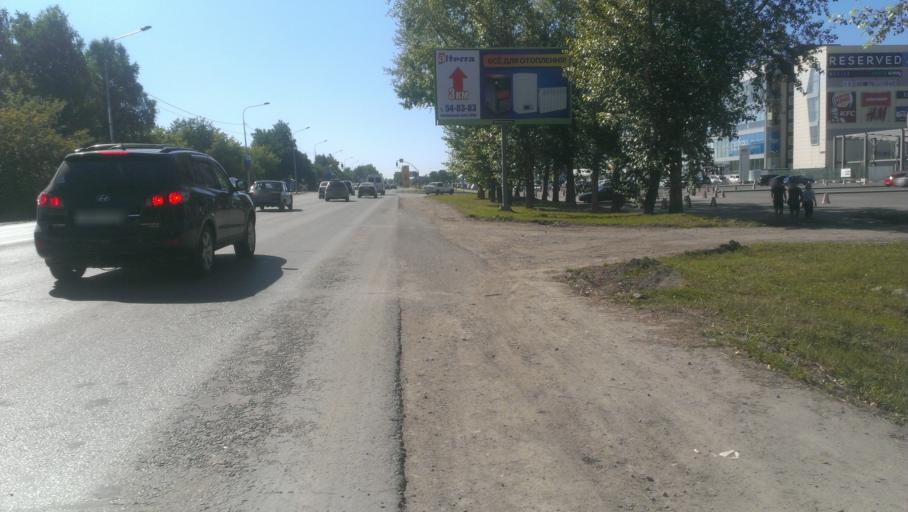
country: RU
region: Altai Krai
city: Novosilikatnyy
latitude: 53.3474
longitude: 83.6408
